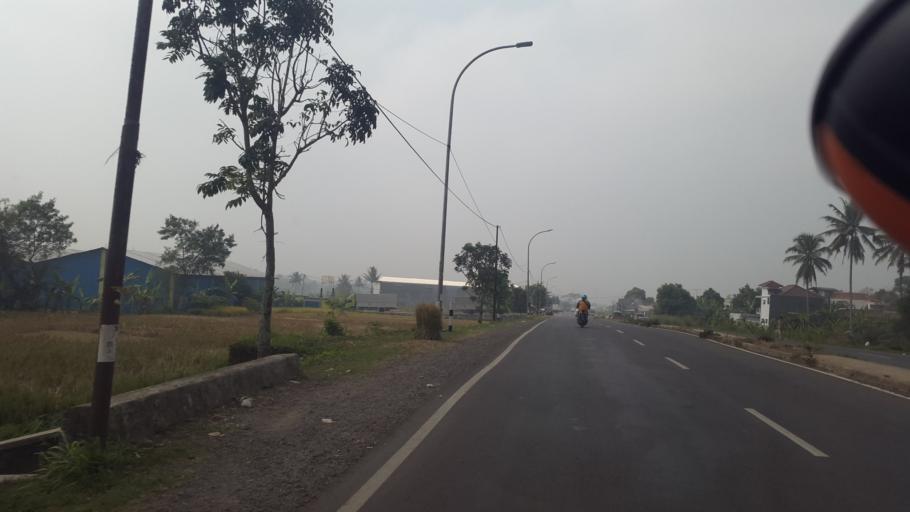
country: ID
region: West Java
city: Sukabumi
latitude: -6.9195
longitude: 106.8880
